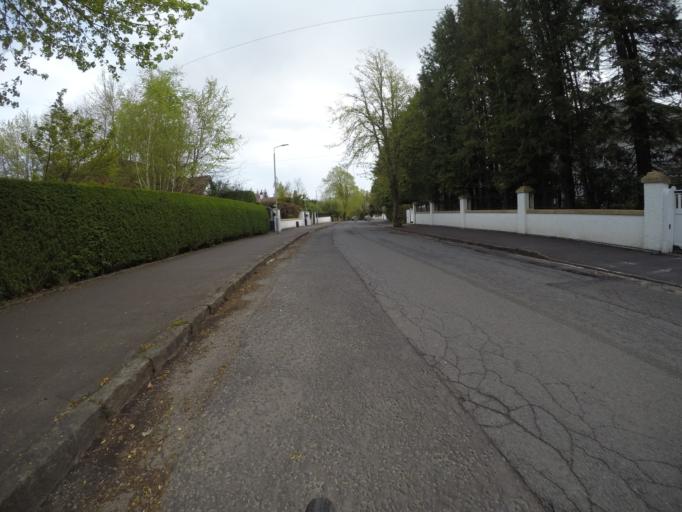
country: GB
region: Scotland
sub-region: East Renfrewshire
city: Giffnock
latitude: 55.7826
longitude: -4.3066
